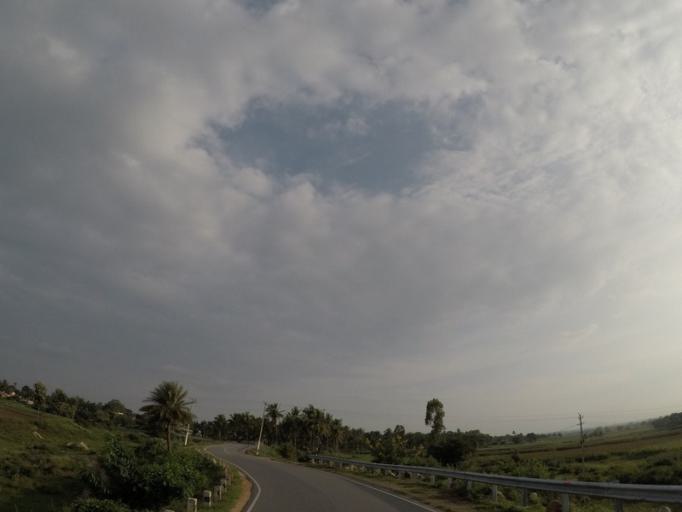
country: IN
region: Karnataka
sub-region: Chikmagalur
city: Chikmagalur
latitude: 13.2638
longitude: 75.8465
